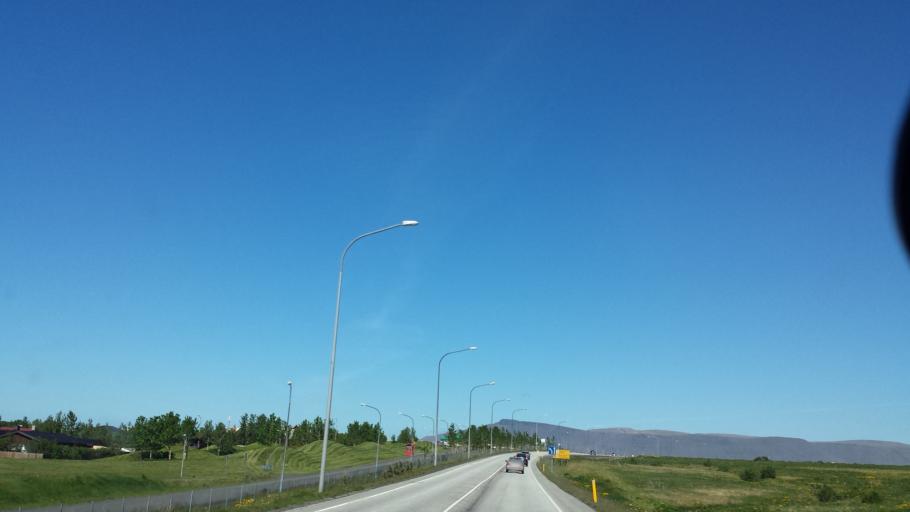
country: IS
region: Capital Region
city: Reykjavik
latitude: 64.2394
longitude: -21.8252
